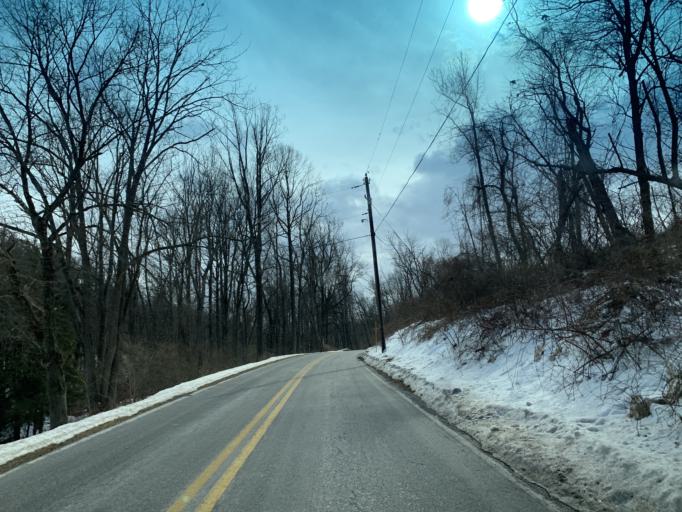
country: US
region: Pennsylvania
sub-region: York County
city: Shrewsbury
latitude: 39.8010
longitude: -76.6558
